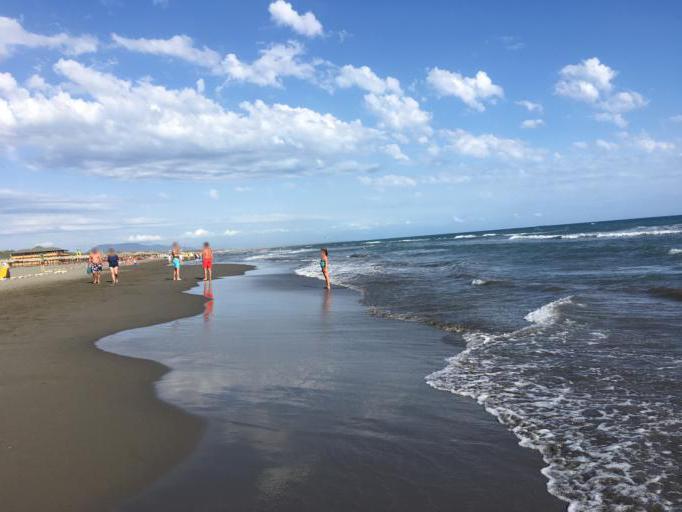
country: ME
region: Ulcinj
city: Ulcinj
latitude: 41.9067
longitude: 19.2501
